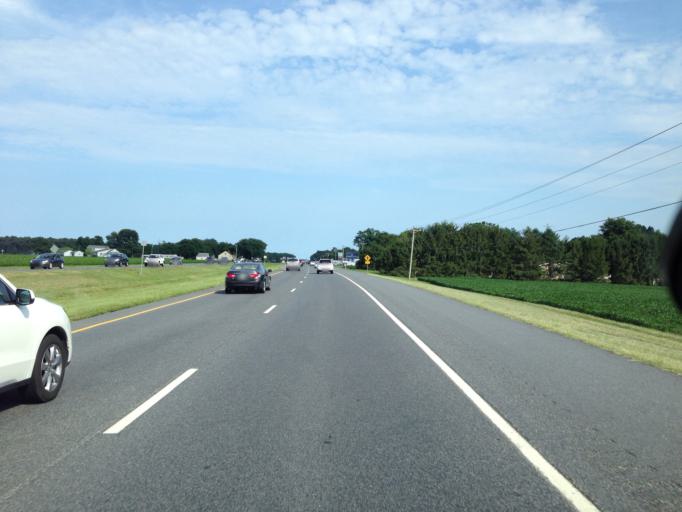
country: US
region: Delaware
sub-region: Sussex County
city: Milton
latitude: 38.8188
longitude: -75.3029
